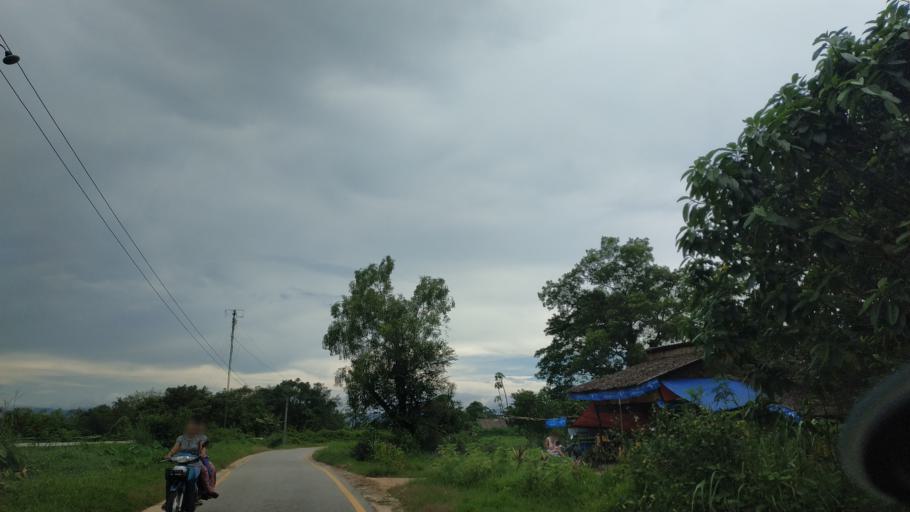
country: MM
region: Tanintharyi
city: Dawei
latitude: 14.0981
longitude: 98.2036
